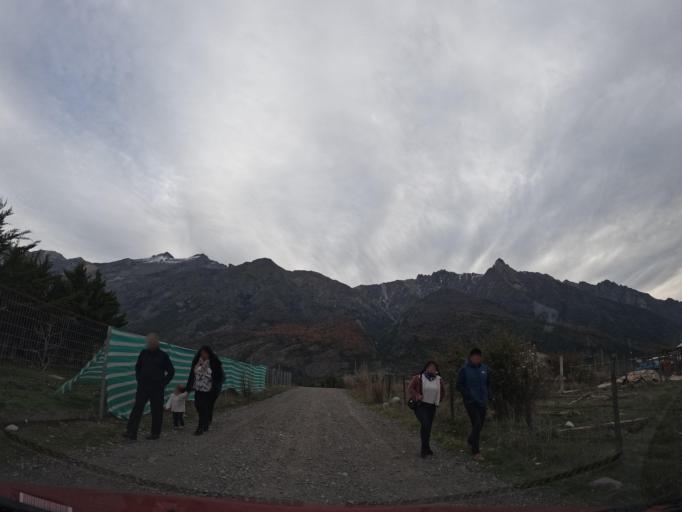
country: CL
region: Maule
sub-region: Provincia de Linares
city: Colbun
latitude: -35.7634
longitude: -70.9987
